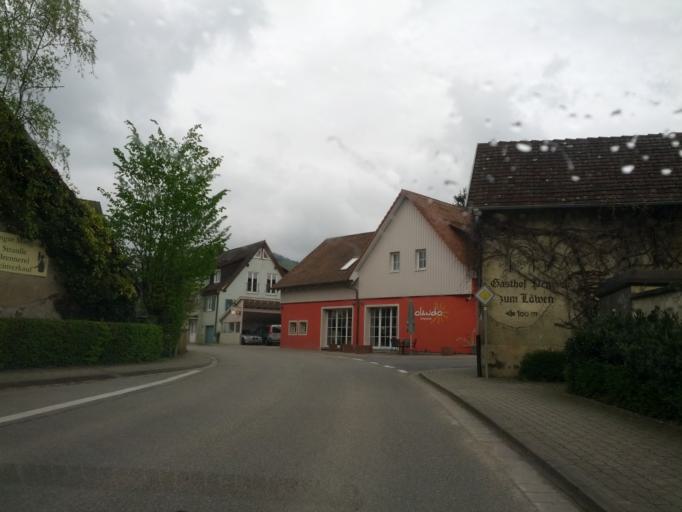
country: DE
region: Baden-Wuerttemberg
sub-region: Freiburg Region
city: Bollschweil
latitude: 47.9203
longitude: 7.7883
